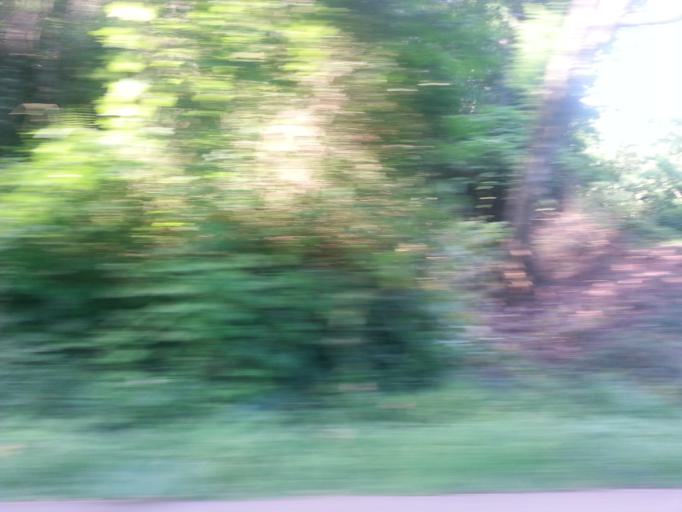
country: US
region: Tennessee
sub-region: Knox County
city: Knoxville
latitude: 35.9195
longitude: -83.9128
